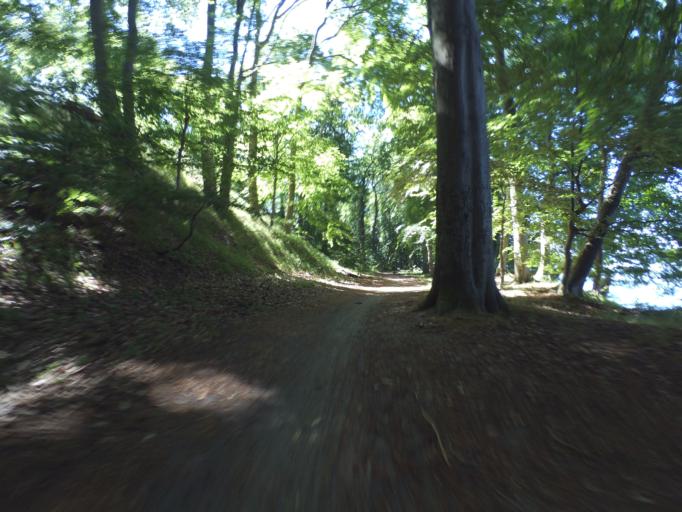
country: DE
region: Mecklenburg-Vorpommern
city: Malchow
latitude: 53.4726
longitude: 12.3489
